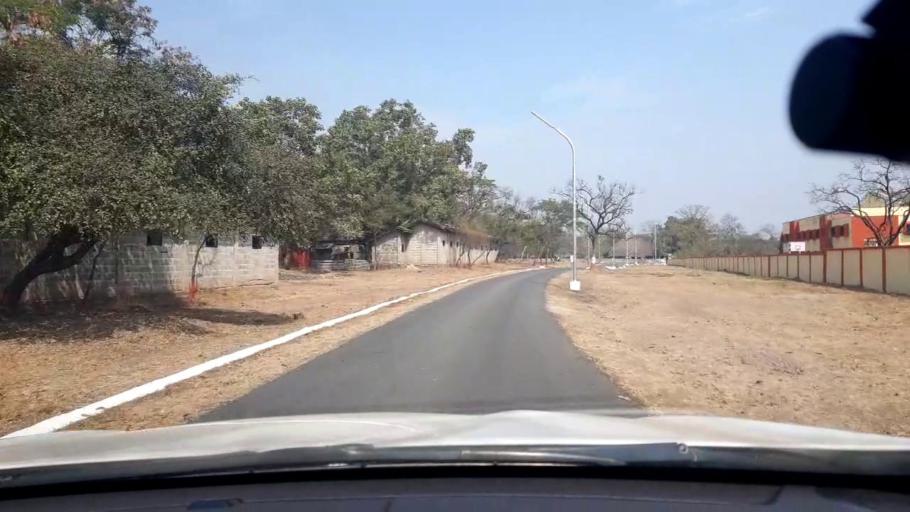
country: IN
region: Maharashtra
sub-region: Pune Division
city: Shivaji Nagar
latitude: 18.5424
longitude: 73.8645
